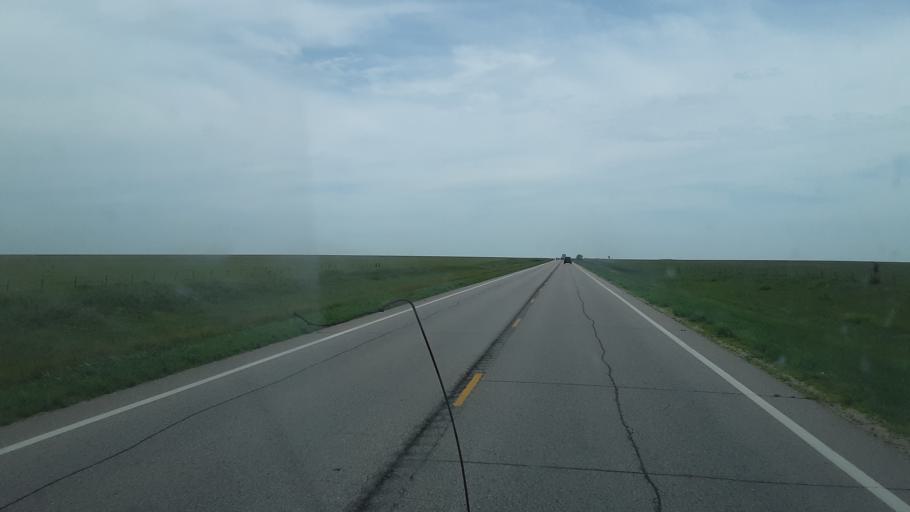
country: US
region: Kansas
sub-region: Butler County
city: El Dorado
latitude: 37.8102
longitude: -96.5811
